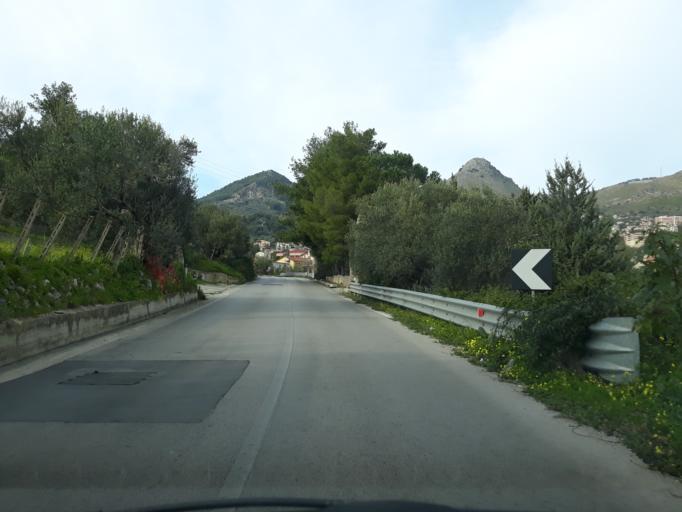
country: IT
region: Sicily
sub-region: Palermo
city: Giardinello
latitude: 38.0818
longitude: 13.1636
